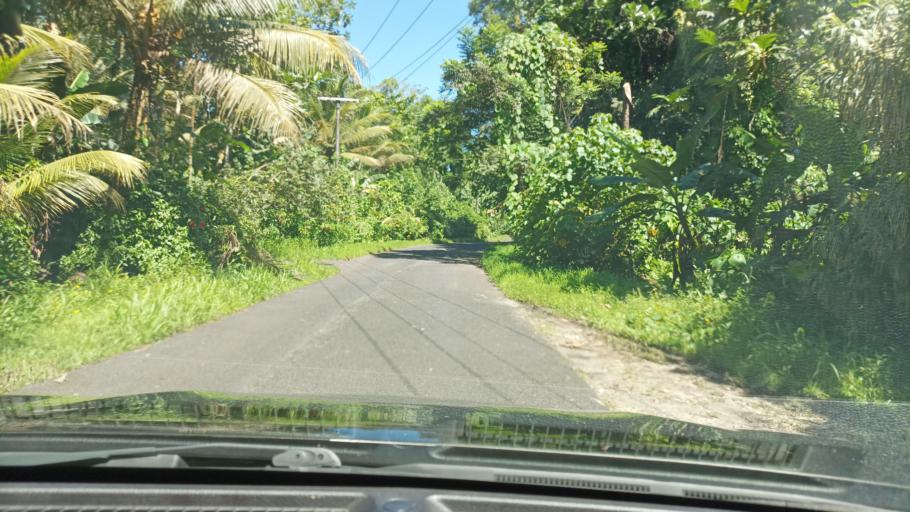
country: FM
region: Pohnpei
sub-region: Madolenihm Municipality
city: Madolenihm Municipality Government
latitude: 6.8519
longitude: 158.2976
